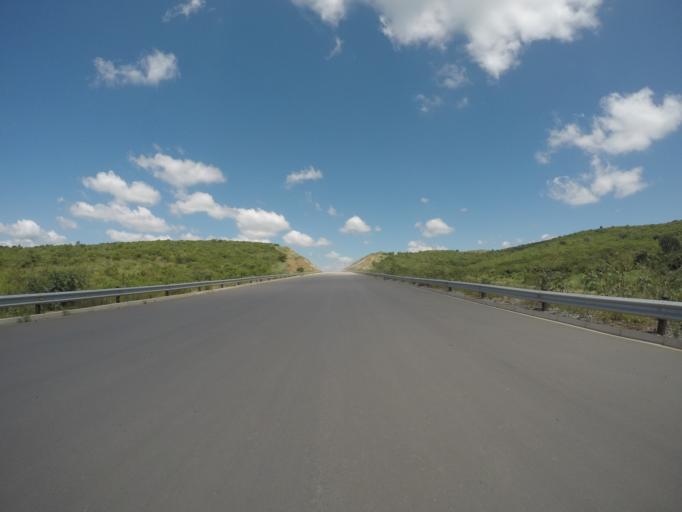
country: ZA
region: KwaZulu-Natal
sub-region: uThungulu District Municipality
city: Empangeni
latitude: -28.6252
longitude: 31.7580
